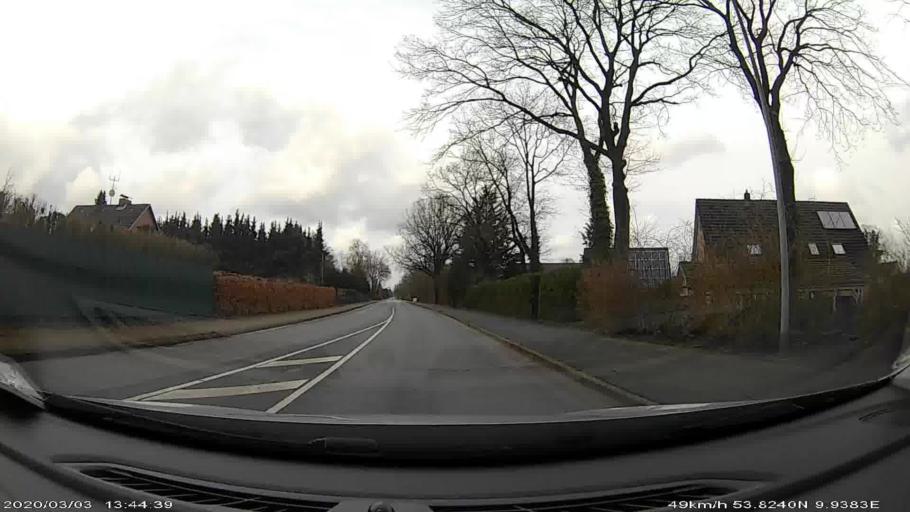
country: DE
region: Schleswig-Holstein
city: Kaltenkirchen
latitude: 53.8246
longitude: 9.9392
